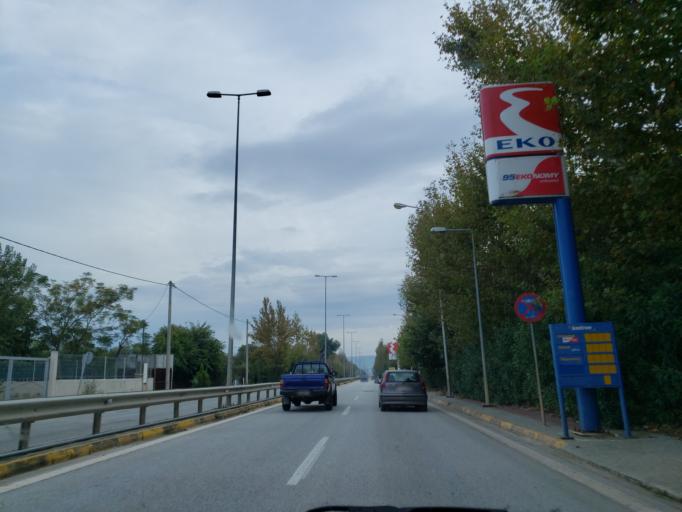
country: GR
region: Attica
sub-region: Nomarchia Anatolikis Attikis
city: Aghios Panteleimon
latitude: 38.1211
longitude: 23.9697
